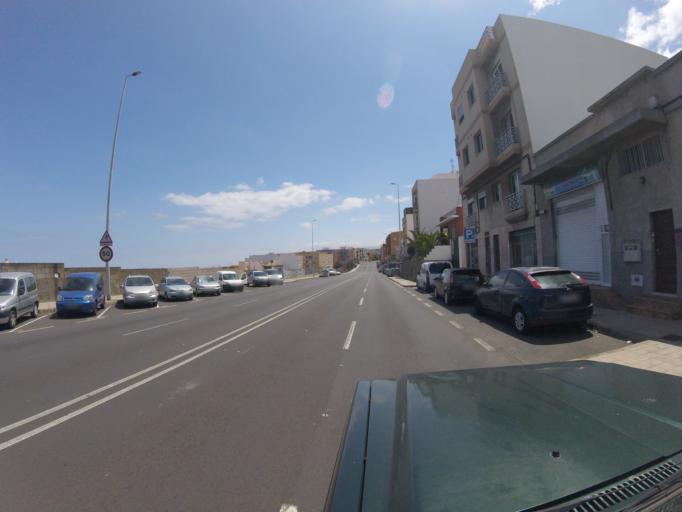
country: ES
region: Canary Islands
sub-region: Provincia de Santa Cruz de Tenerife
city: La Laguna
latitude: 28.4371
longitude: -16.3065
